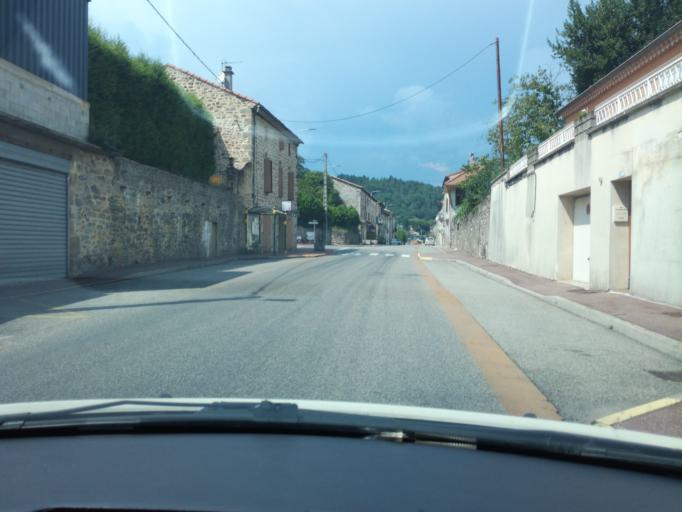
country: FR
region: Rhone-Alpes
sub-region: Departement de l'Ardeche
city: Labegude
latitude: 44.6380
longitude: 4.3733
